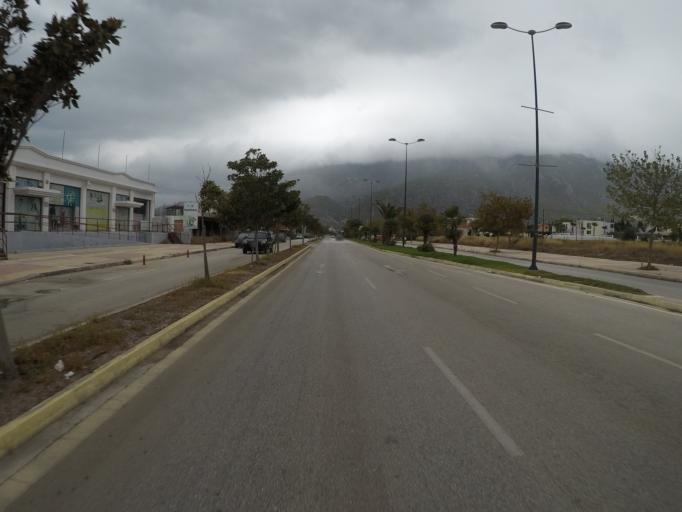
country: GR
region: Peloponnese
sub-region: Nomos Korinthias
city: Loutraki
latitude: 37.9620
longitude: 22.9787
